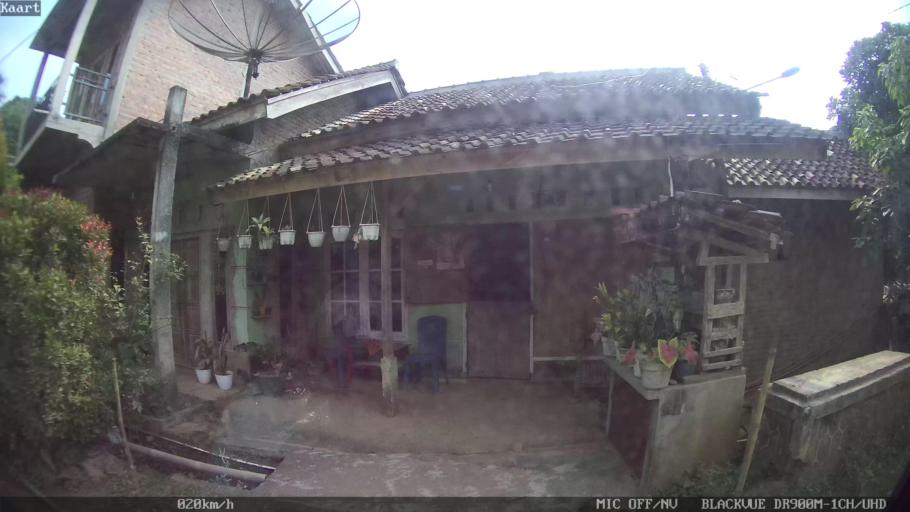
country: ID
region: Lampung
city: Gadingrejo
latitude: -5.3903
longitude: 105.0205
